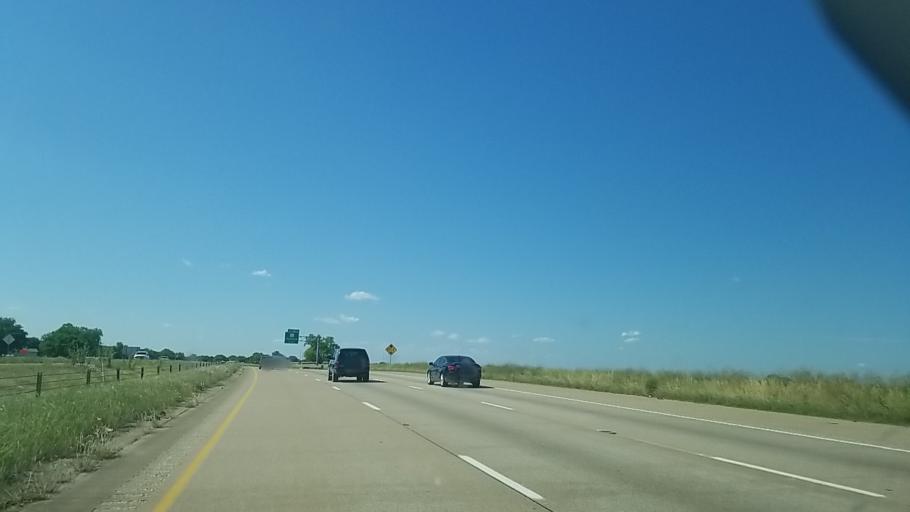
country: US
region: Texas
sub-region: Ellis County
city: Palmer
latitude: 32.4761
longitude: -96.6616
